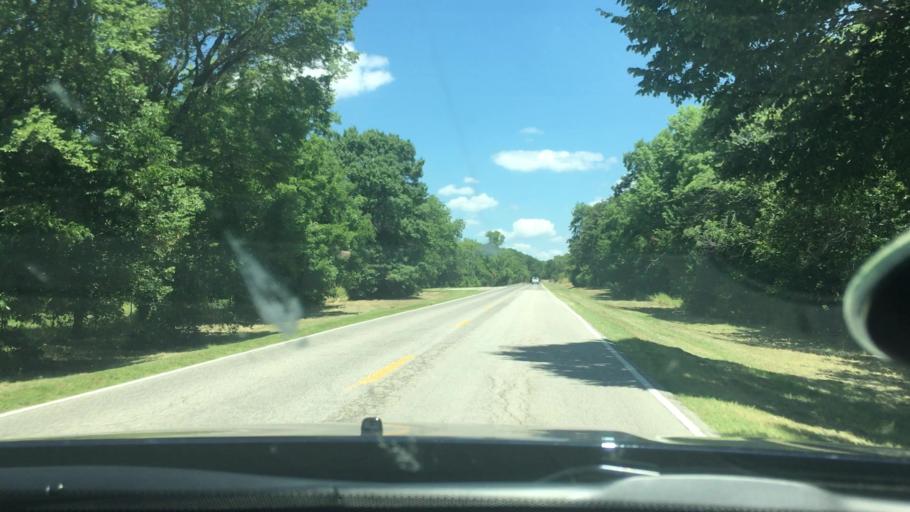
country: US
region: Oklahoma
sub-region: Carter County
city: Dickson
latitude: 34.3095
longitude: -96.9628
